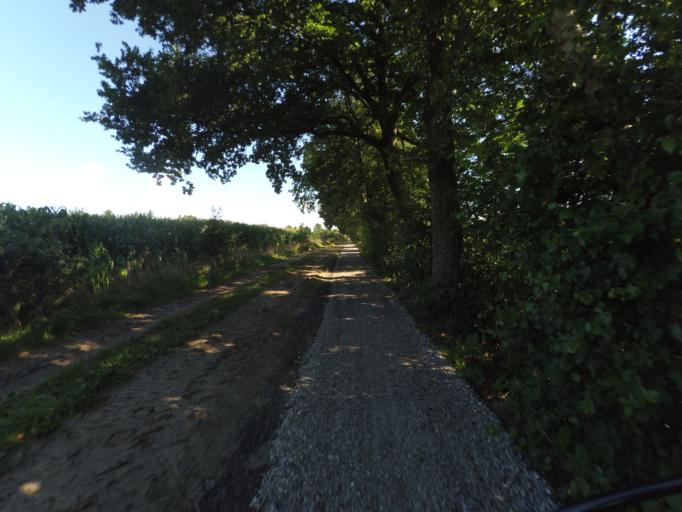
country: NL
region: Friesland
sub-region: Gemeente Kollumerland en Nieuwkruisland
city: Kollumerzwaag
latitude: 53.2699
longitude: 6.1013
